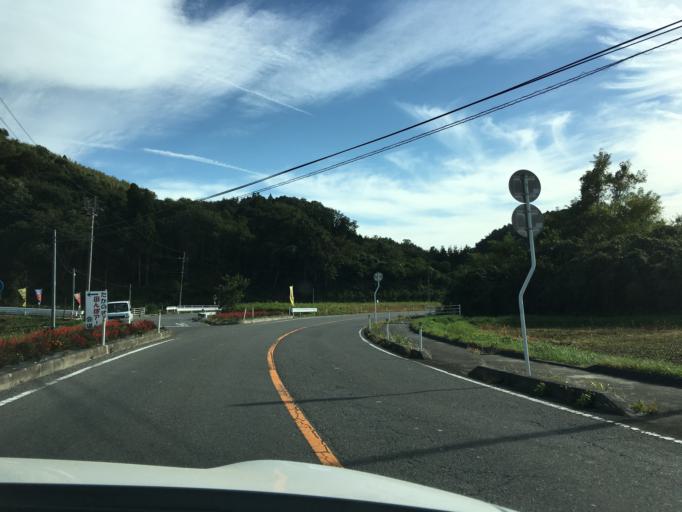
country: JP
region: Fukushima
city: Miharu
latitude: 37.4134
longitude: 140.4616
